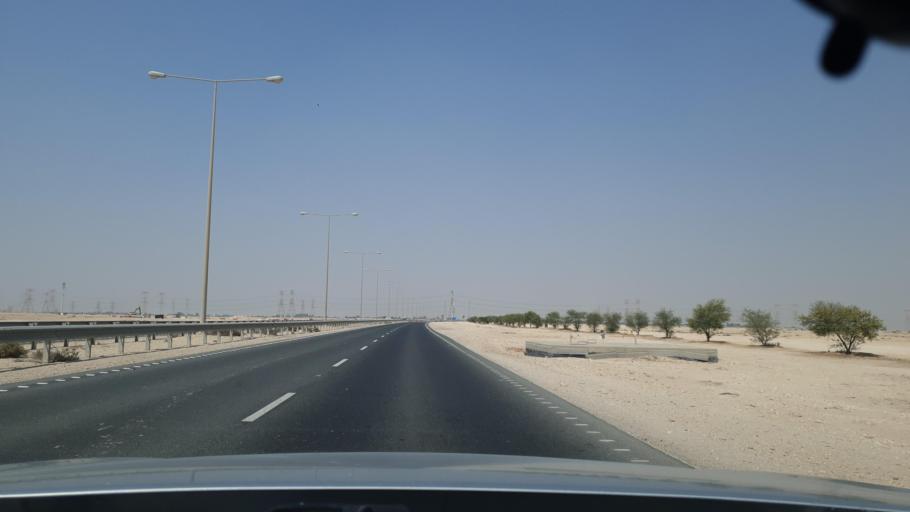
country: QA
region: Al Khawr
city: Al Khawr
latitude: 25.7453
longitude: 51.4823
